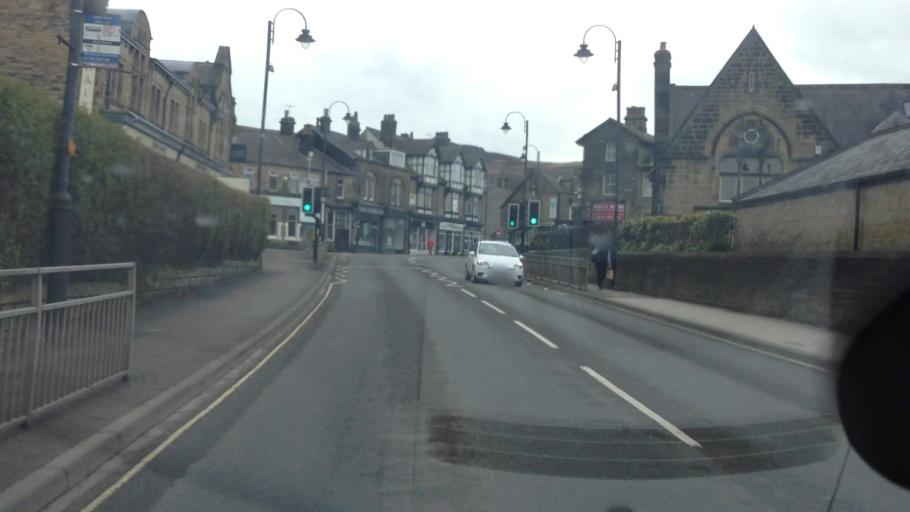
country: GB
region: England
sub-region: Bradford
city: Ilkley
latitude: 53.9271
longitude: -1.8199
